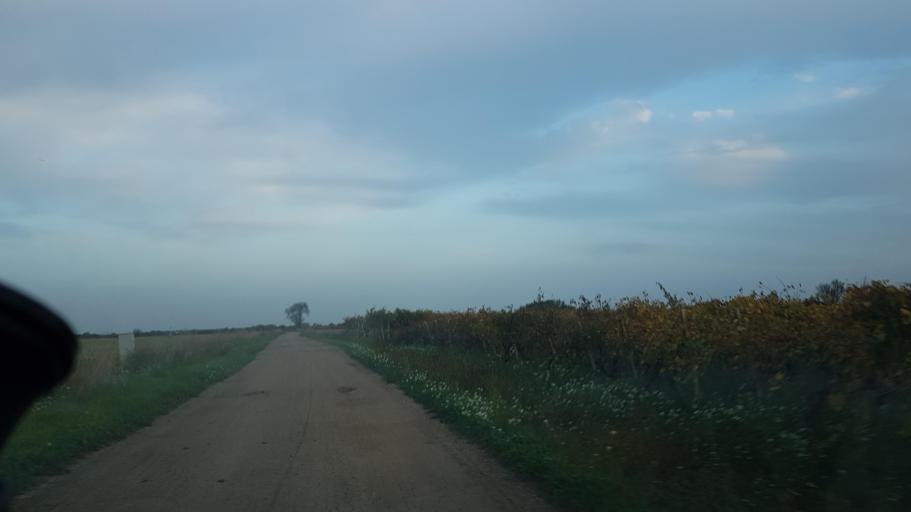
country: IT
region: Apulia
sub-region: Provincia di Brindisi
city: San Donaci
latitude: 40.4265
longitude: 17.9190
